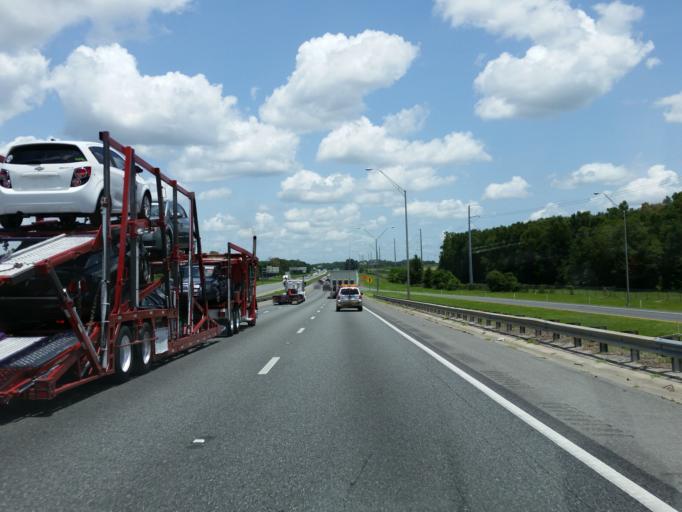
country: US
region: Florida
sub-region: Marion County
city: Ocala
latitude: 29.2084
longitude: -82.1844
